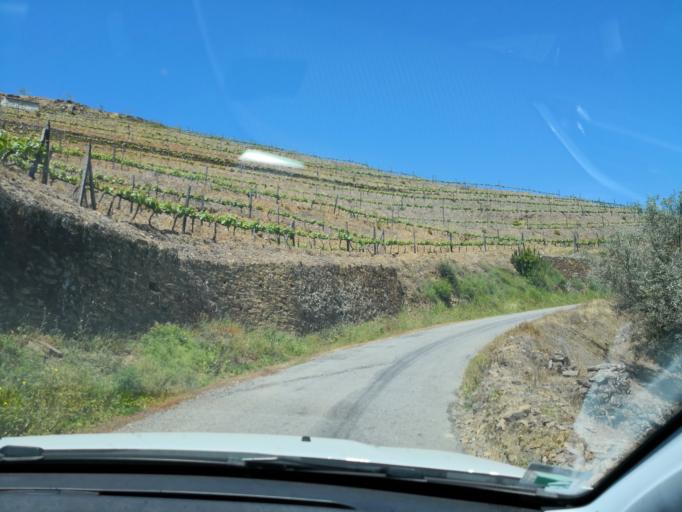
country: PT
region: Vila Real
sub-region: Vila Real
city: Vila Real
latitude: 41.2314
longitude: -7.7205
